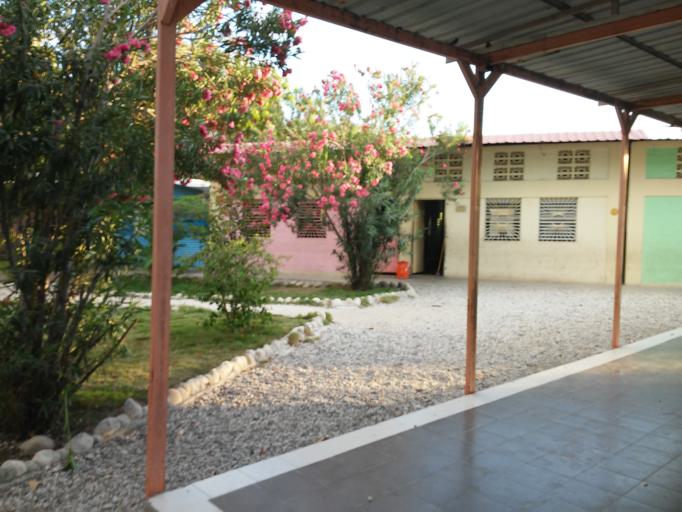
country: HT
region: Ouest
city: Port-au-Prince
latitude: 18.5680
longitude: -72.3492
